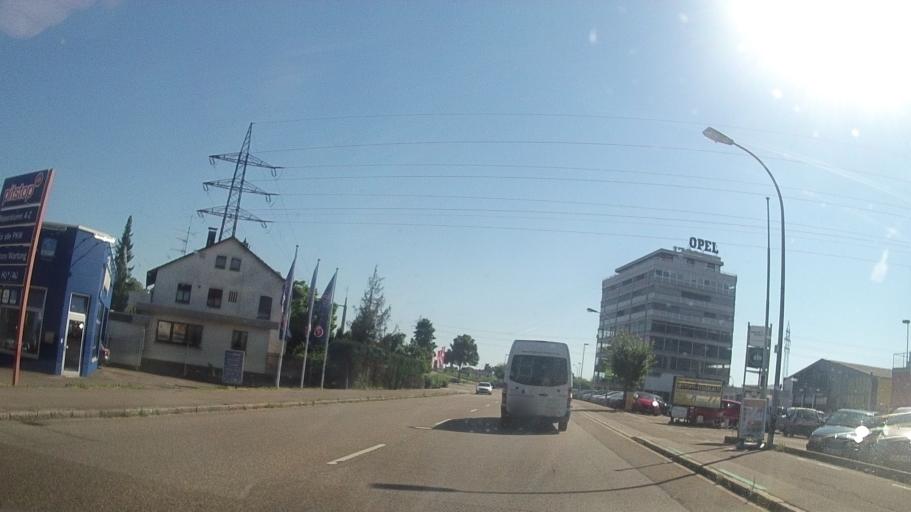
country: DE
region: Baden-Wuerttemberg
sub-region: Freiburg Region
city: Offenburg
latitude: 48.4740
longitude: 7.9348
